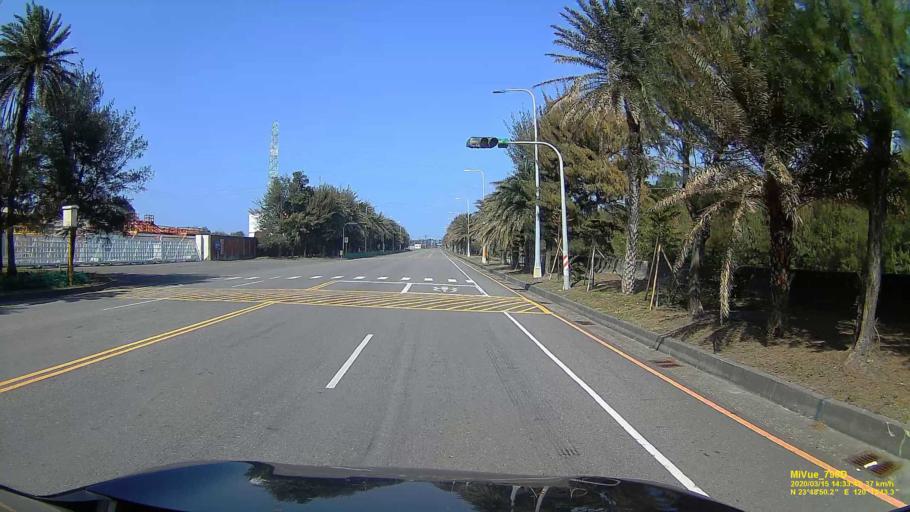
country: TW
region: Taiwan
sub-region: Yunlin
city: Douliu
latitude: 23.8140
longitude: 120.2288
